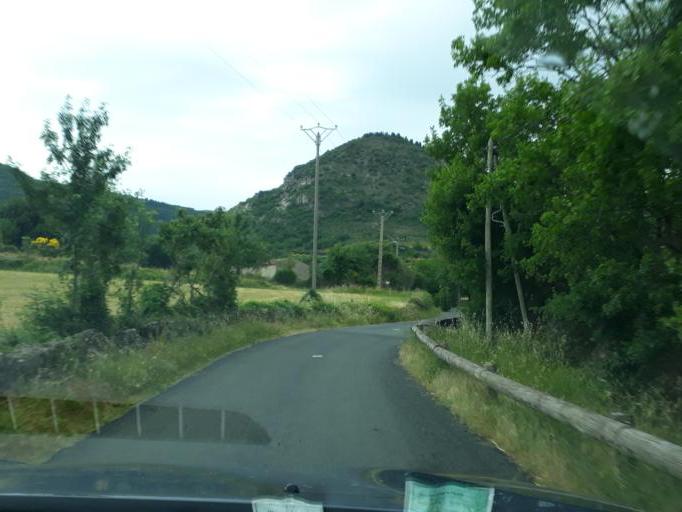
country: FR
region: Languedoc-Roussillon
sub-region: Departement de l'Herault
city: Lodeve
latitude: 43.7766
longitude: 3.2921
